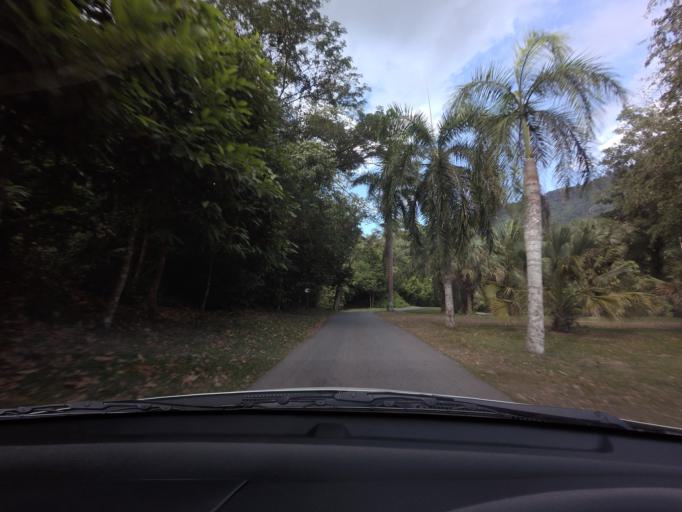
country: TH
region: Nakhon Nayok
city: Nakhon Nayok
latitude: 14.3338
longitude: 101.3047
